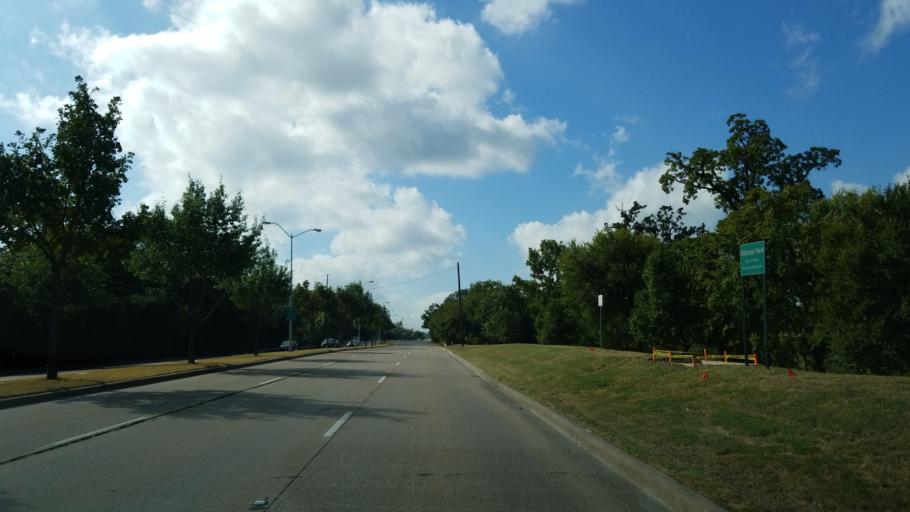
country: US
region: Texas
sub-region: Dallas County
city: Addison
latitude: 32.9369
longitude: -96.7863
